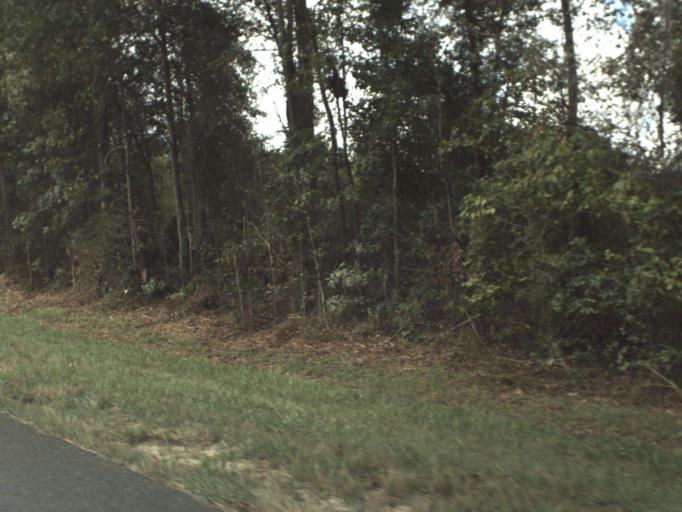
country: US
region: Florida
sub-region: Washington County
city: Chipley
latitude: 30.8111
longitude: -85.5107
